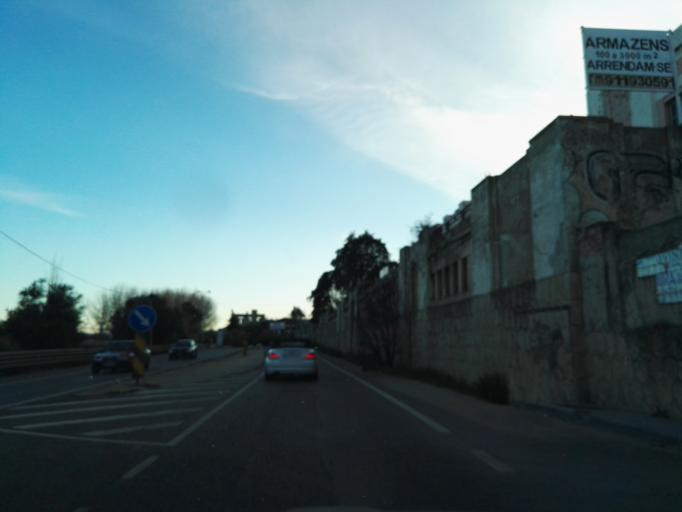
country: PT
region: Lisbon
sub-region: Loures
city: Santa Iria da Azoia
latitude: 38.8496
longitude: -9.0759
